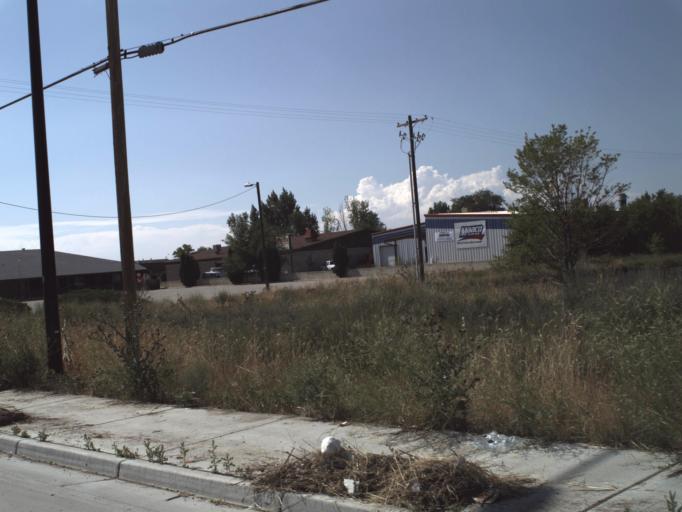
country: US
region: Utah
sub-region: Weber County
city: Ogden
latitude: 41.2444
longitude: -111.9836
